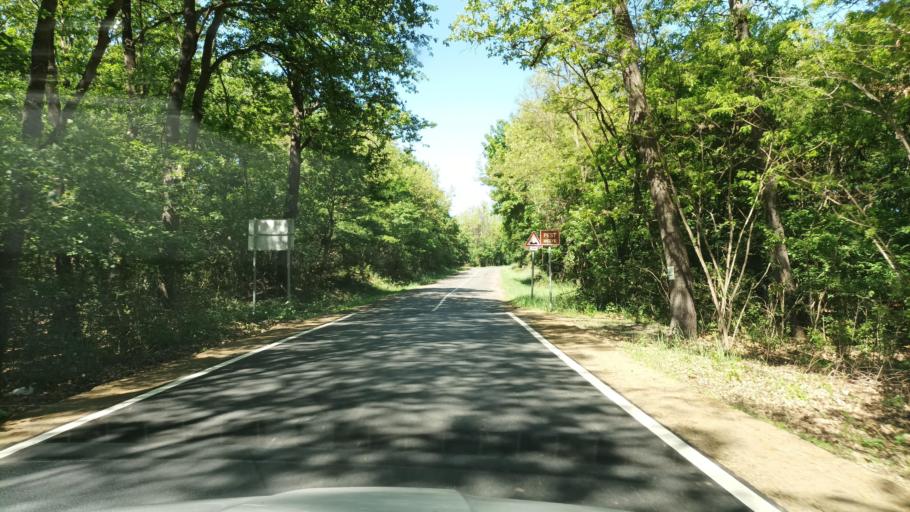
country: HU
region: Pest
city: Acsa
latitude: 47.7845
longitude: 19.4235
